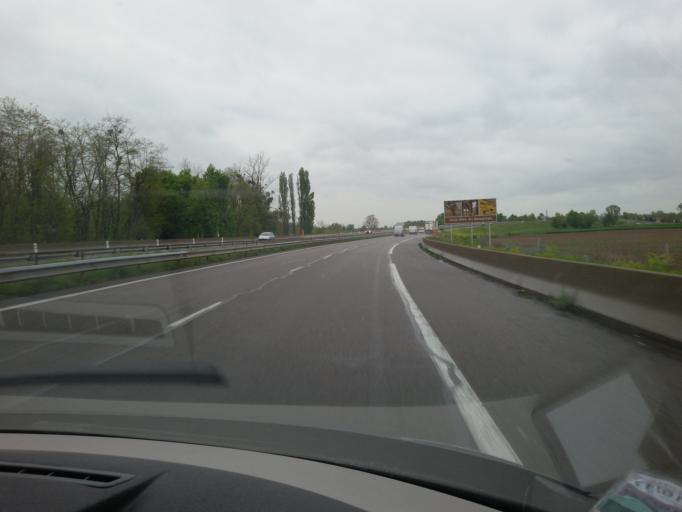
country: FR
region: Rhone-Alpes
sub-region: Departement du Rhone
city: Anse
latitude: 45.9221
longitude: 4.7254
